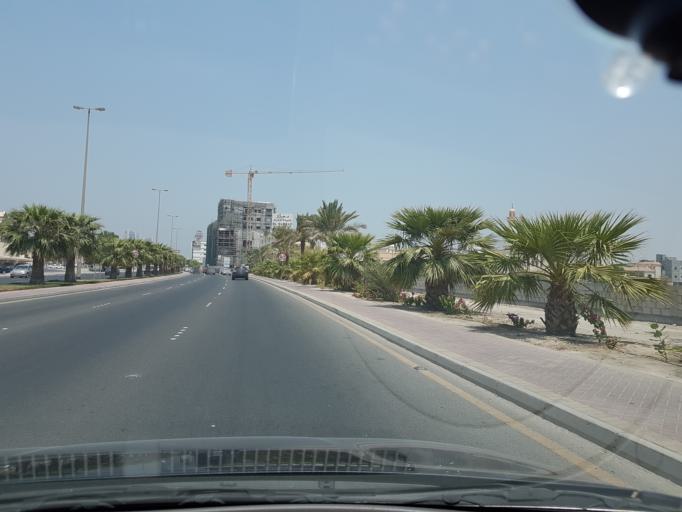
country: BH
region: Manama
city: Manama
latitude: 26.2062
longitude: 50.5677
